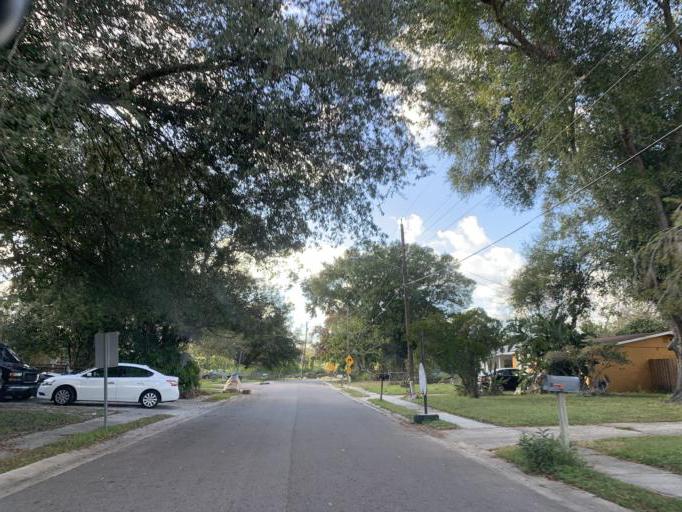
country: US
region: Florida
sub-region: Orange County
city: Eatonville
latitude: 28.6146
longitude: -81.3931
